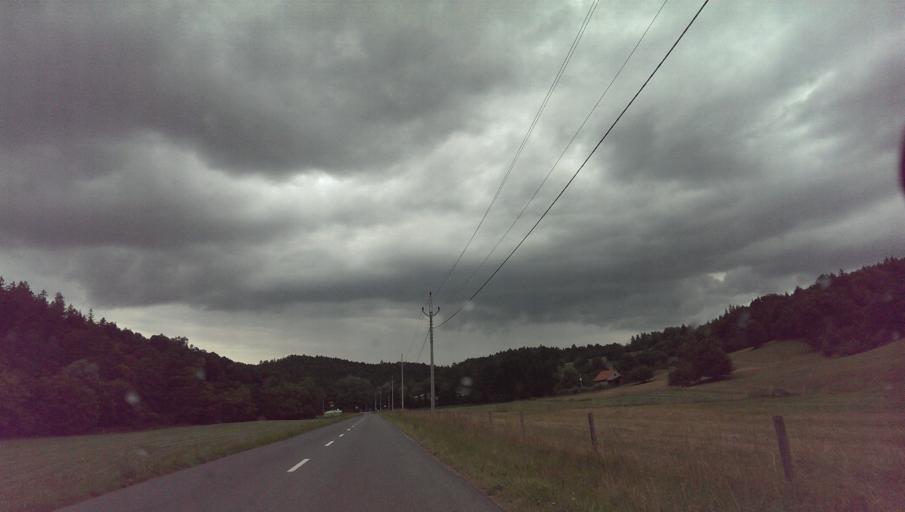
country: CZ
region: South Moravian
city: Velka nad Velickou
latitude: 48.8903
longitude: 17.5766
